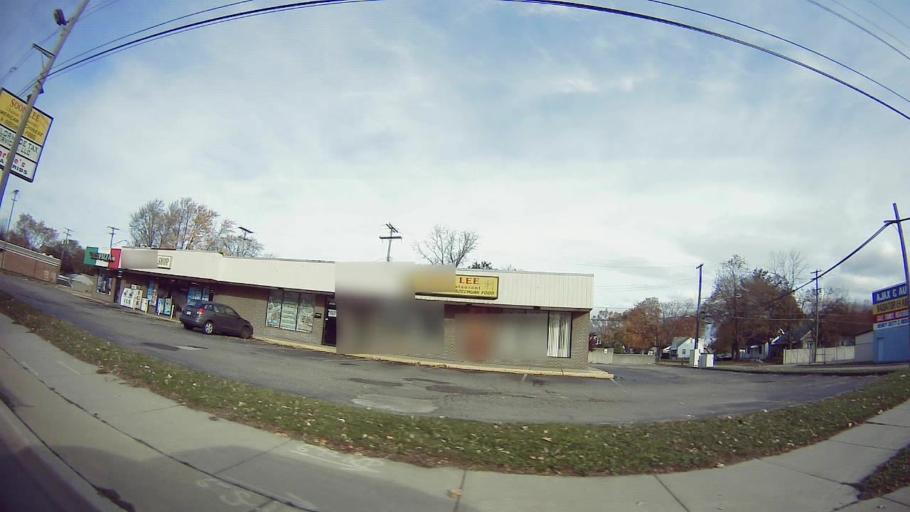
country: US
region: Michigan
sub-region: Macomb County
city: Eastpointe
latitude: 42.4644
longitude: -82.9732
